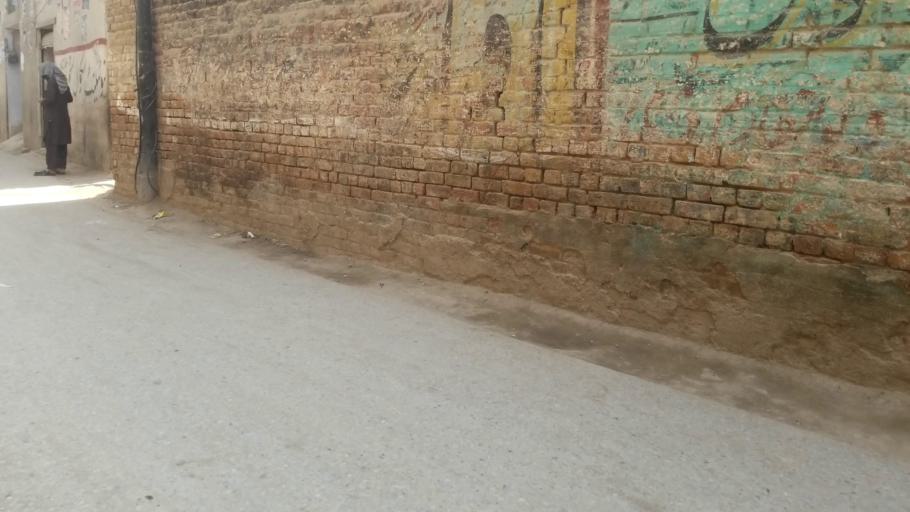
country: PK
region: Khyber Pakhtunkhwa
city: Peshawar
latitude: 33.9913
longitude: 71.5443
